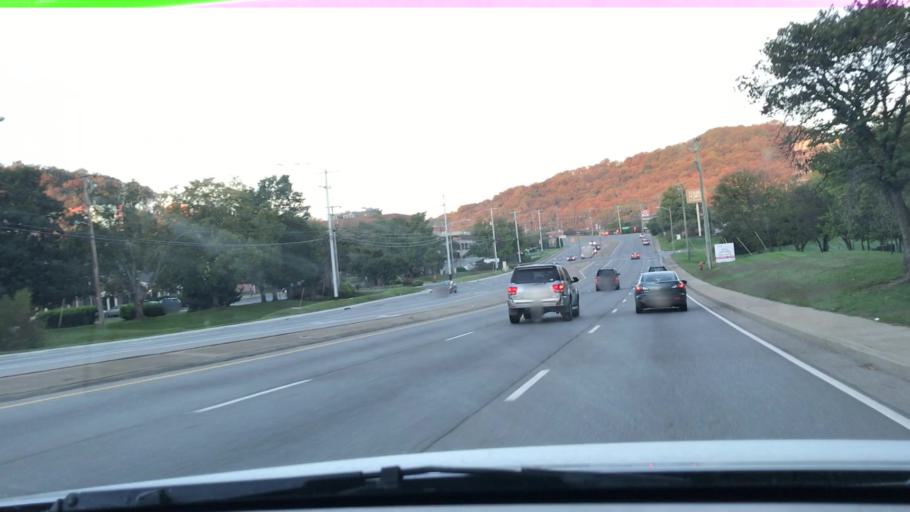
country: US
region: Tennessee
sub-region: Williamson County
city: Brentwood
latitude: 36.0410
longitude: -86.7738
